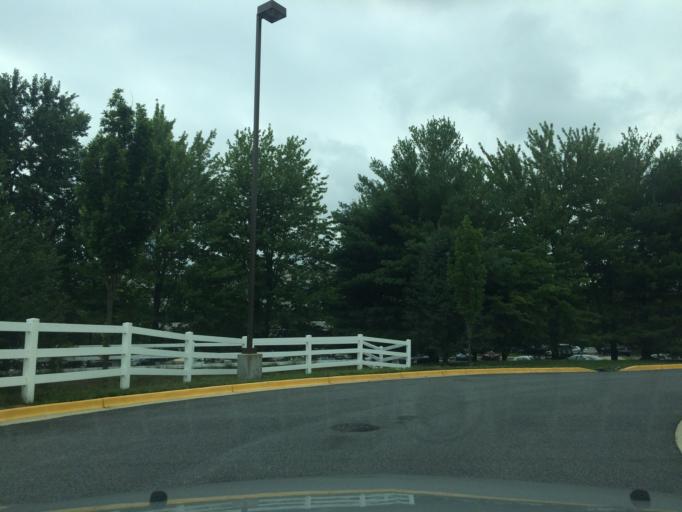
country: US
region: Maryland
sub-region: Prince George's County
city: Lake Arbor
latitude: 38.9076
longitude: -76.8464
